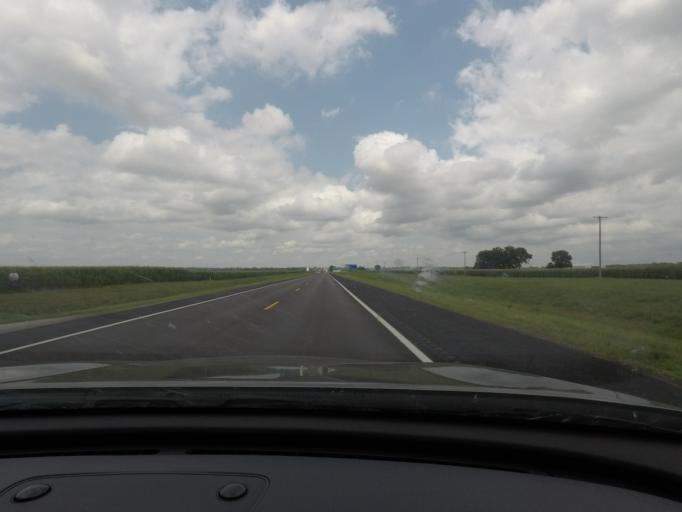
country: US
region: Missouri
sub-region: Carroll County
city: Carrollton
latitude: 39.3233
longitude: -93.4957
